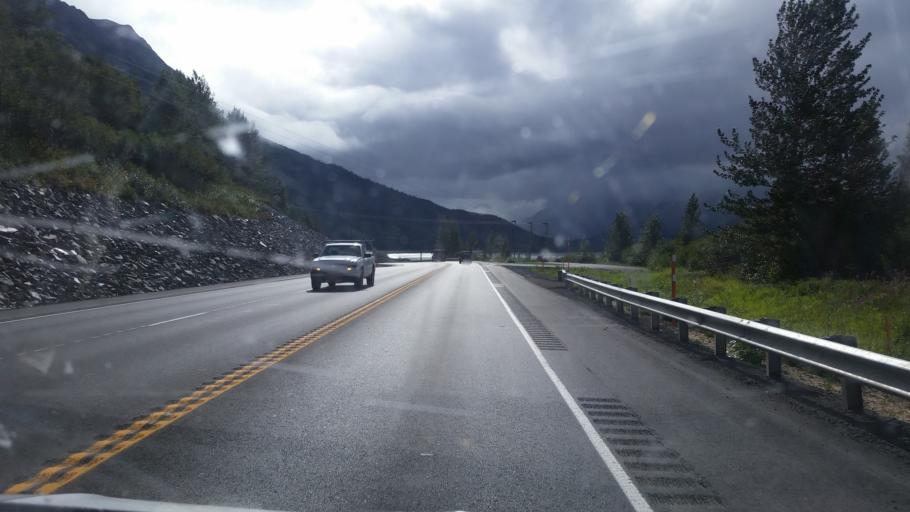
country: US
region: Alaska
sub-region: Anchorage Municipality
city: Girdwood
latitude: 60.9531
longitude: -149.4129
